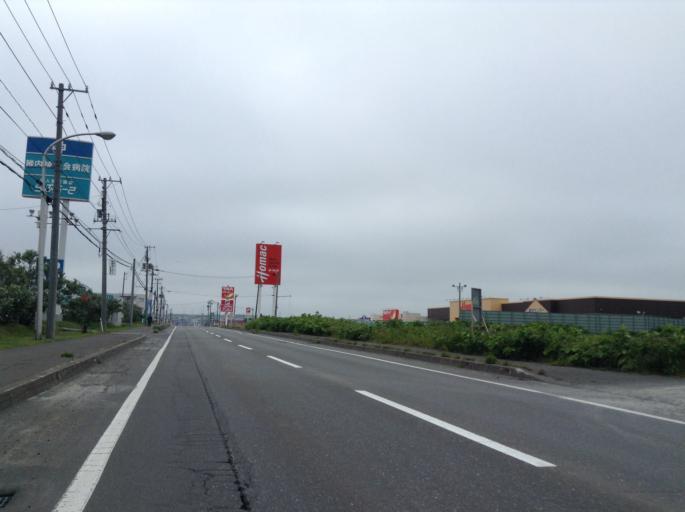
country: JP
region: Hokkaido
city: Wakkanai
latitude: 45.3865
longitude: 141.6957
